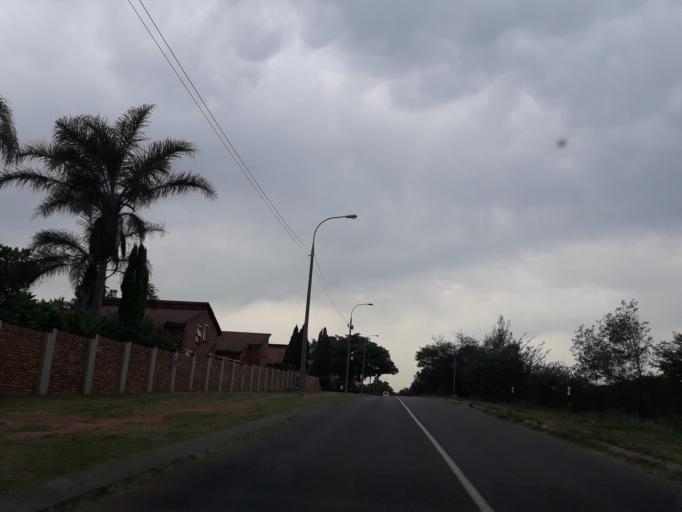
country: ZA
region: Gauteng
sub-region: City of Johannesburg Metropolitan Municipality
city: Roodepoort
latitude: -26.1086
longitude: 27.9179
